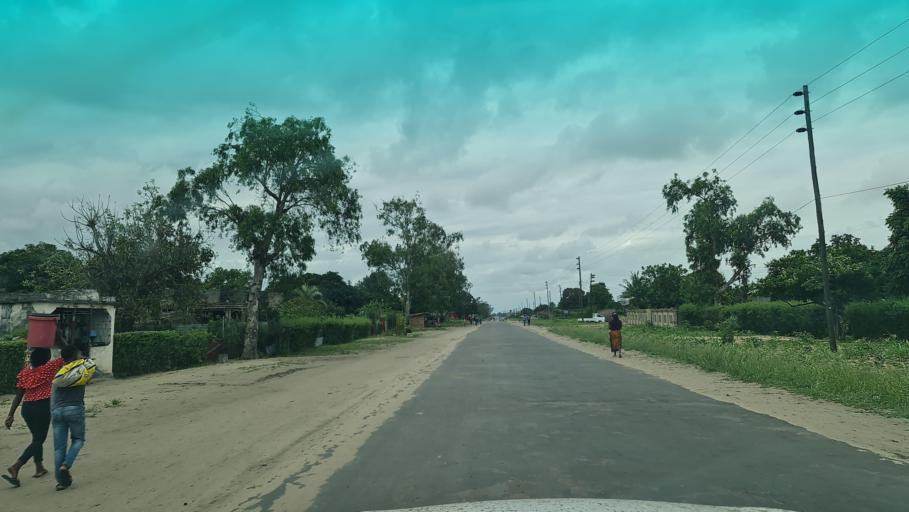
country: MZ
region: Maputo
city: Manhica
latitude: -25.4433
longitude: 32.7737
